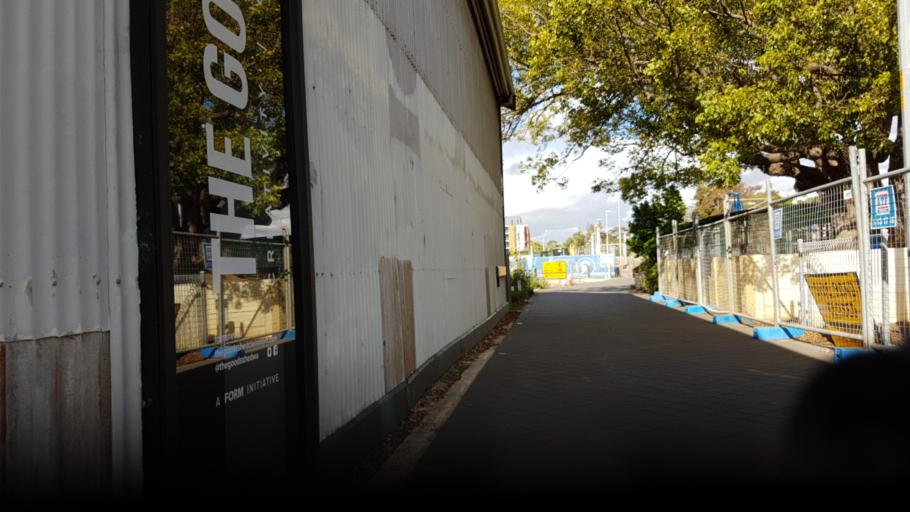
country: AU
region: Western Australia
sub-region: Claremont
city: Claremont
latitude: -31.9807
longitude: 115.7810
